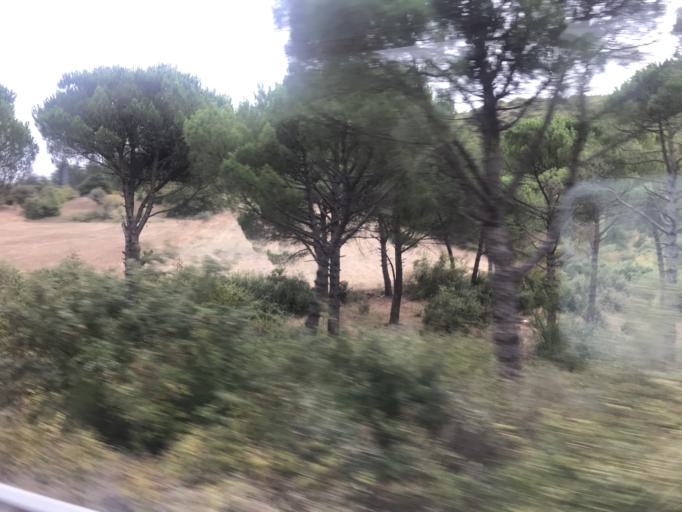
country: TR
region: Balikesir
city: Ergama
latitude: 39.6212
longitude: 27.5835
